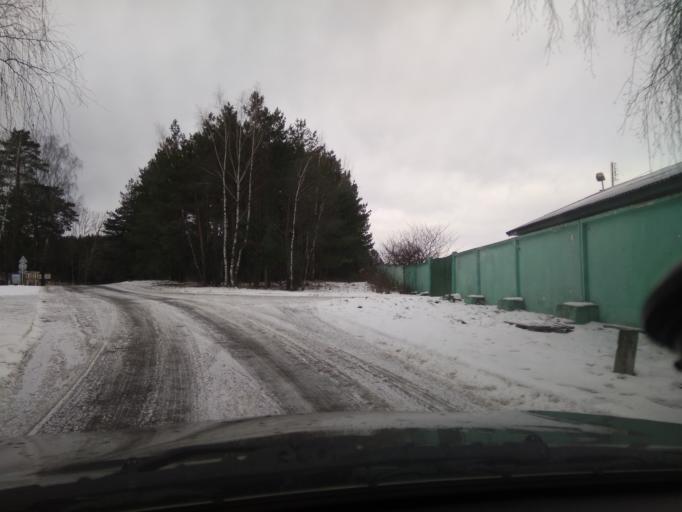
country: BY
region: Minsk
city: Borovlyany
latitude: 53.9617
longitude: 27.6495
